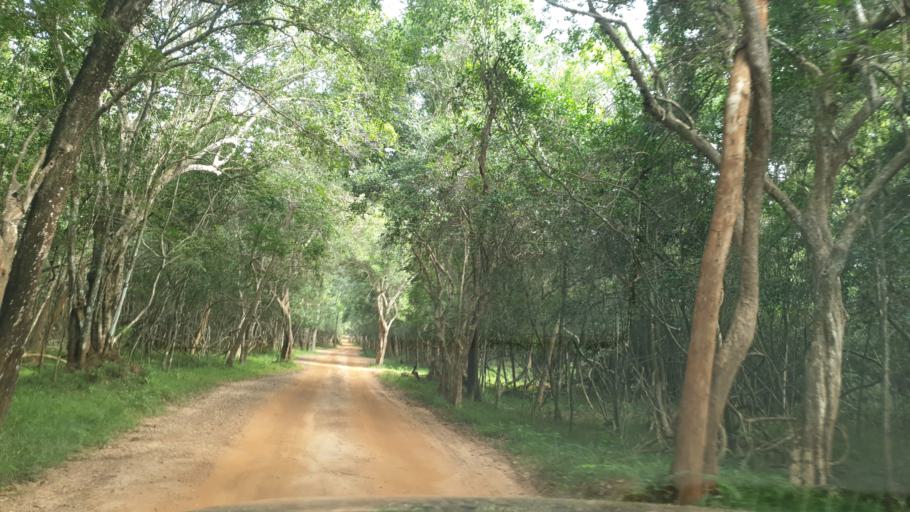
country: LK
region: North Central
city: Anuradhapura
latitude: 8.4104
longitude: 80.0389
